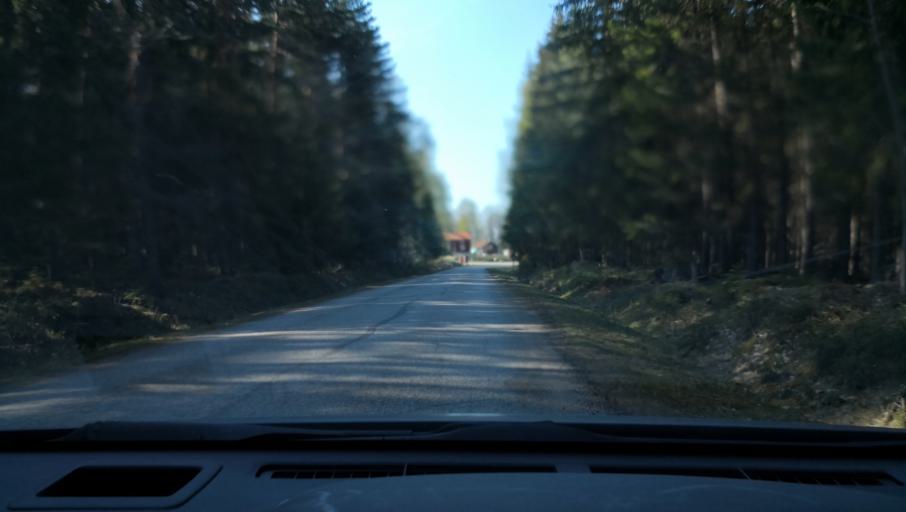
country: SE
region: Uppsala
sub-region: Heby Kommun
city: Tarnsjo
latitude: 60.2818
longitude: 16.8855
